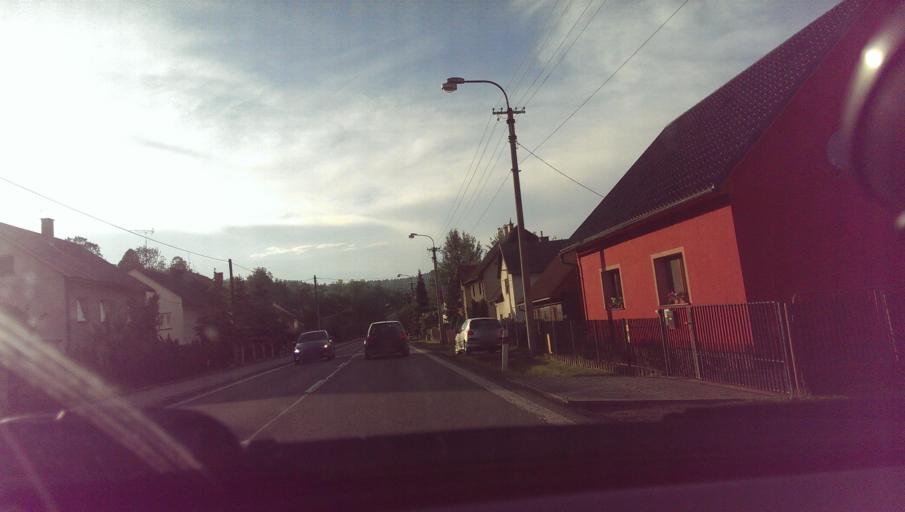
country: CZ
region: Zlin
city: Valasska Polanka
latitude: 49.2519
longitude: 17.9997
